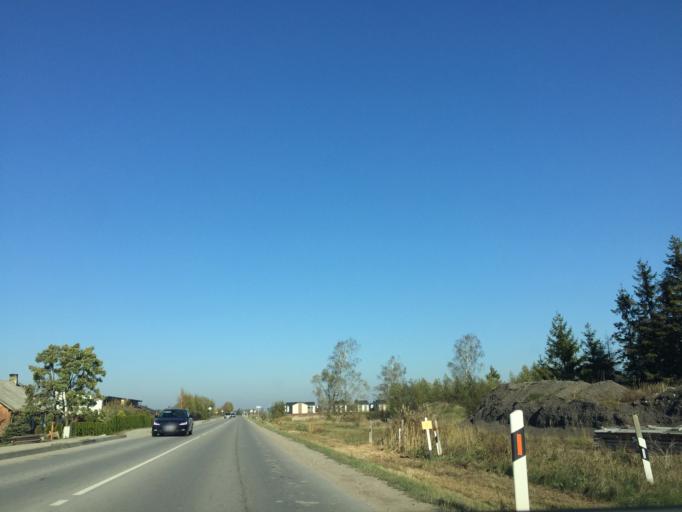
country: LT
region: Klaipedos apskritis
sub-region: Klaipeda
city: Klaipeda
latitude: 55.7372
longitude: 21.1928
